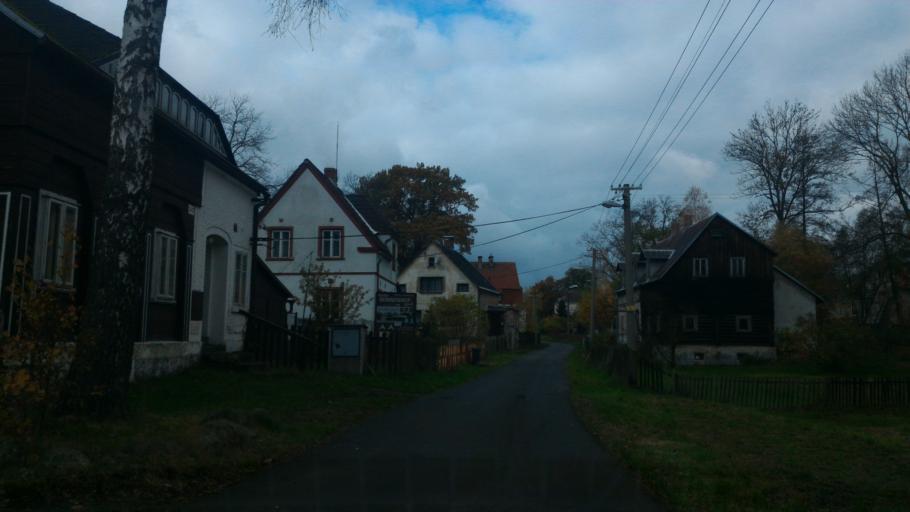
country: CZ
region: Ustecky
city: Dolni Podluzi
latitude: 50.8814
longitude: 14.5618
